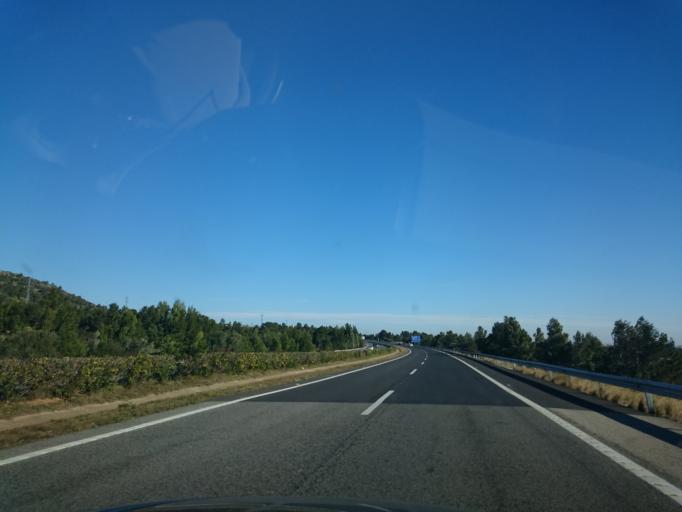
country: ES
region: Catalonia
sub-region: Provincia de Tarragona
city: Colldejou
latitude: 40.9917
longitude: 0.9033
